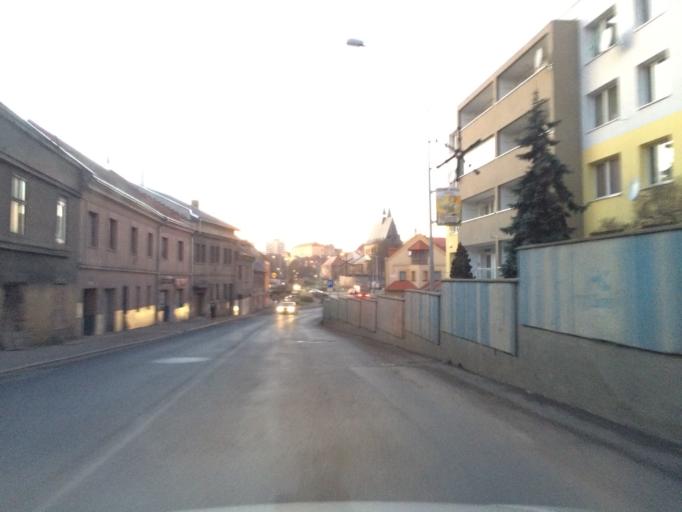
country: CZ
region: Central Bohemia
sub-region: Okres Kladno
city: Slany
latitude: 50.2286
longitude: 14.0939
